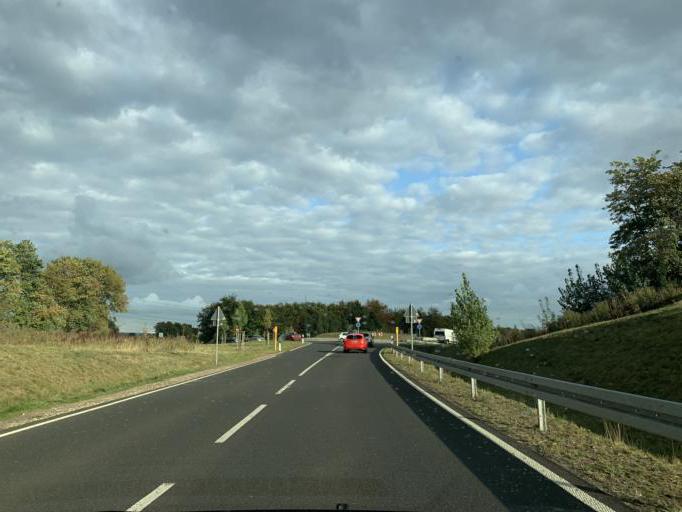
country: DE
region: North Rhine-Westphalia
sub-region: Regierungsbezirk Koln
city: Aldenhoven
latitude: 50.9154
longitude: 6.3203
